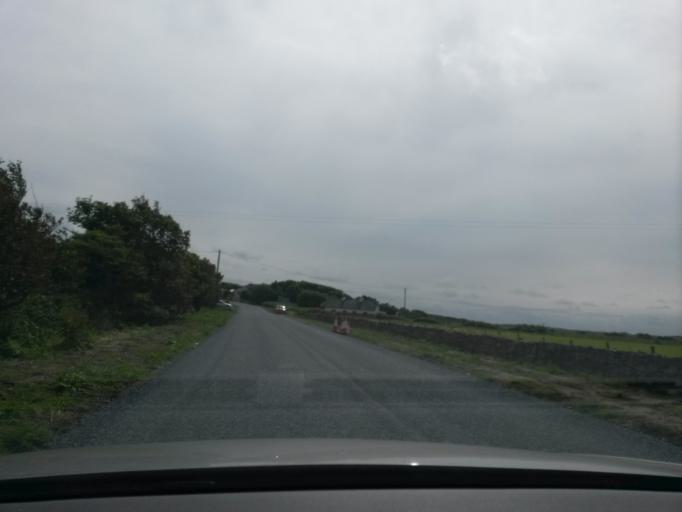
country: IE
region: Connaught
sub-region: Sligo
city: Sligo
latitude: 54.4352
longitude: -8.4567
